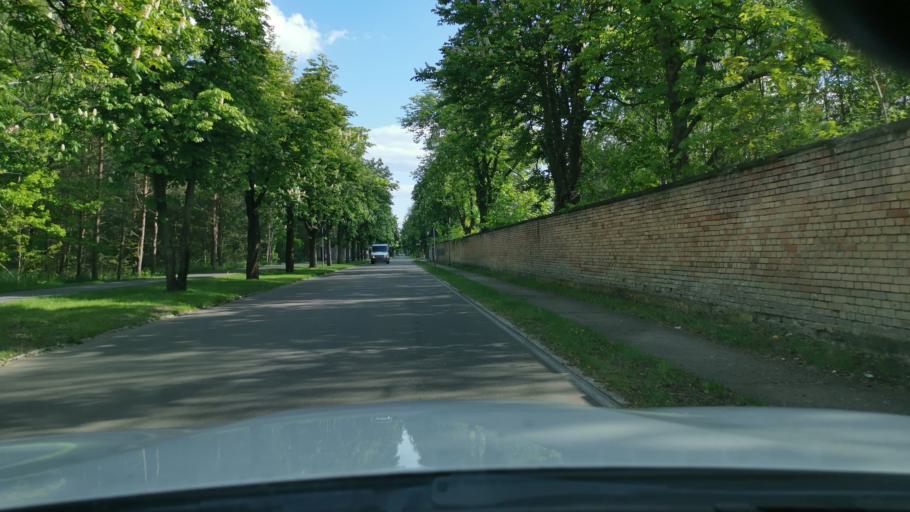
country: DE
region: Brandenburg
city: Niedergorsdorf
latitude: 52.0140
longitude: 12.9934
